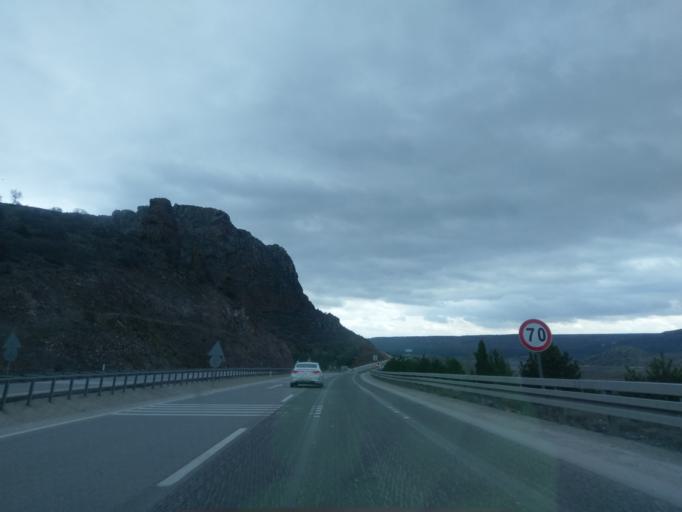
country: TR
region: Kuetahya
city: Sabuncu
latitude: 39.5763
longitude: 30.0896
